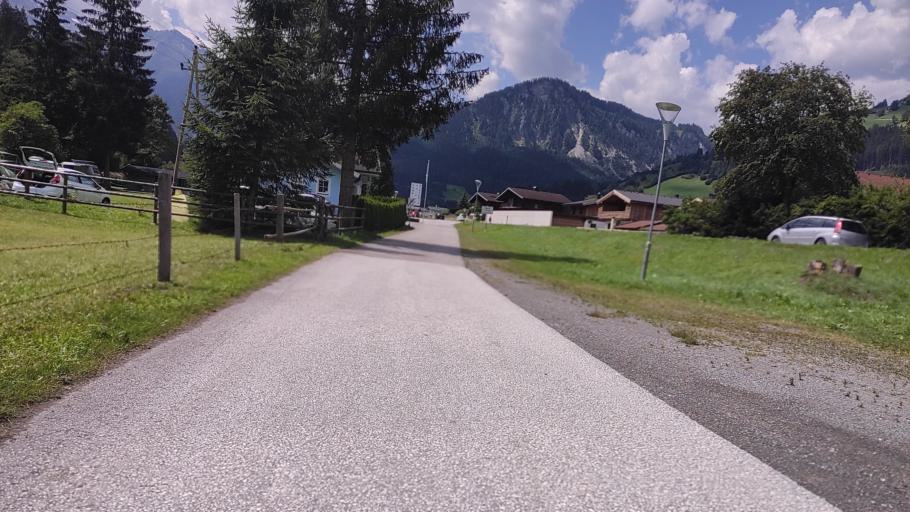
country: AT
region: Salzburg
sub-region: Politischer Bezirk Zell am See
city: Wald im Pinzgau
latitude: 47.2425
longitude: 12.2117
